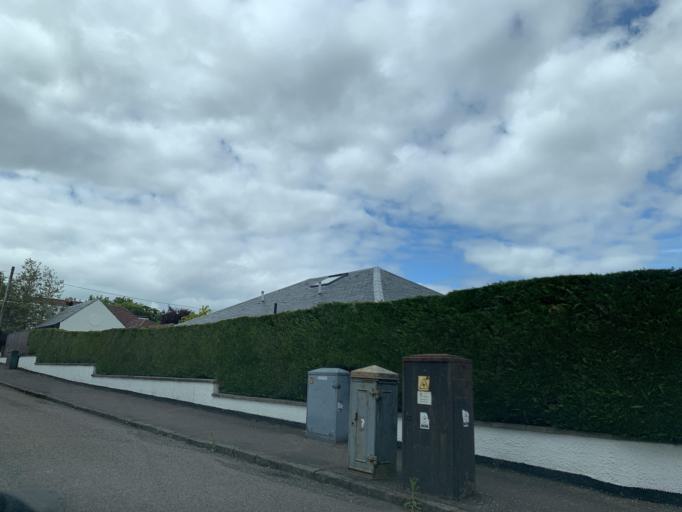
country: GB
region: Scotland
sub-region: East Renfrewshire
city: Newton Mearns
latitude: 55.7731
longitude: -4.3269
